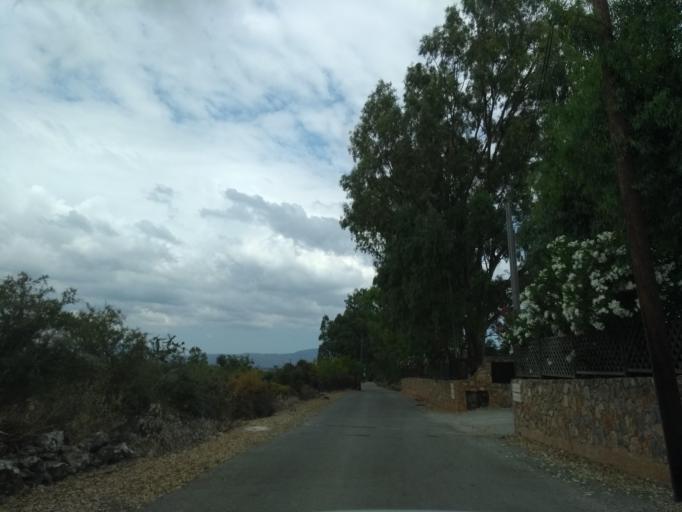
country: GR
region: Crete
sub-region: Nomos Chanias
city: Kalivai
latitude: 35.4055
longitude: 24.2164
